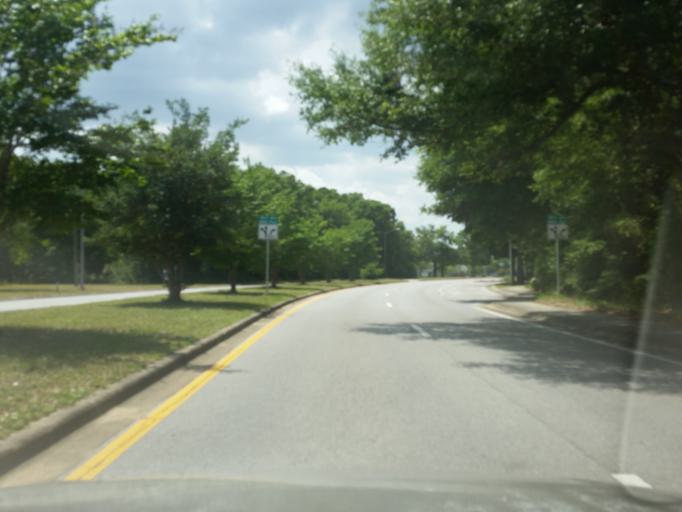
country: US
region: Florida
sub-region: Escambia County
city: Goulding
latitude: 30.4669
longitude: -87.1999
